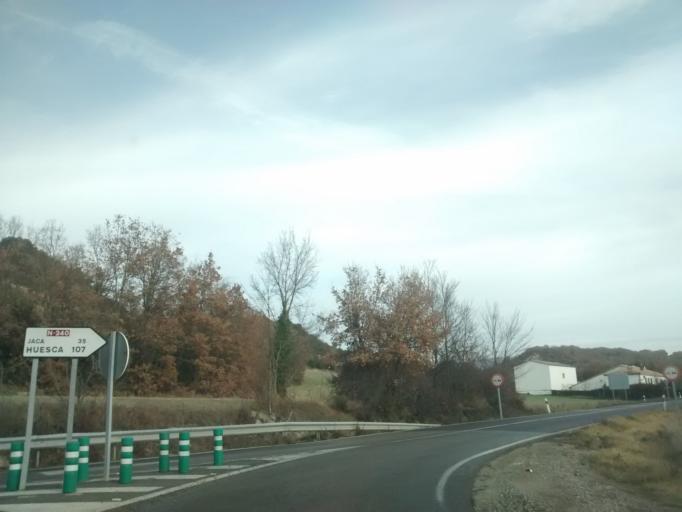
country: ES
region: Aragon
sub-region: Provincia de Zaragoza
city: Mianos
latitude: 42.6127
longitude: -0.9063
